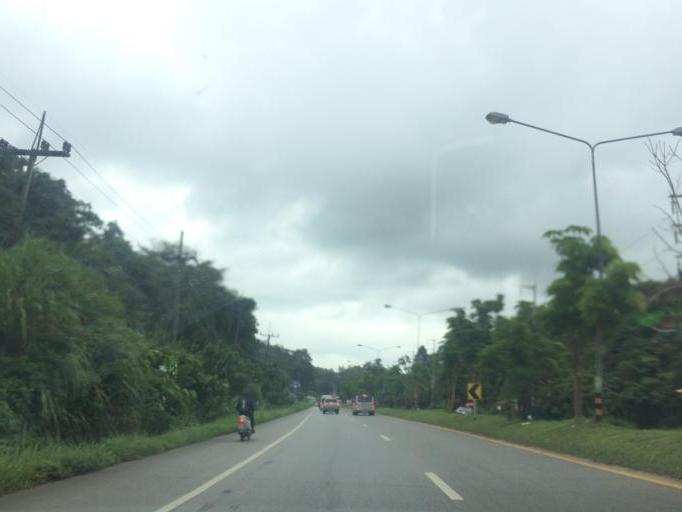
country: TH
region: Chiang Rai
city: Mae Chan
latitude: 20.1162
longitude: 99.8722
